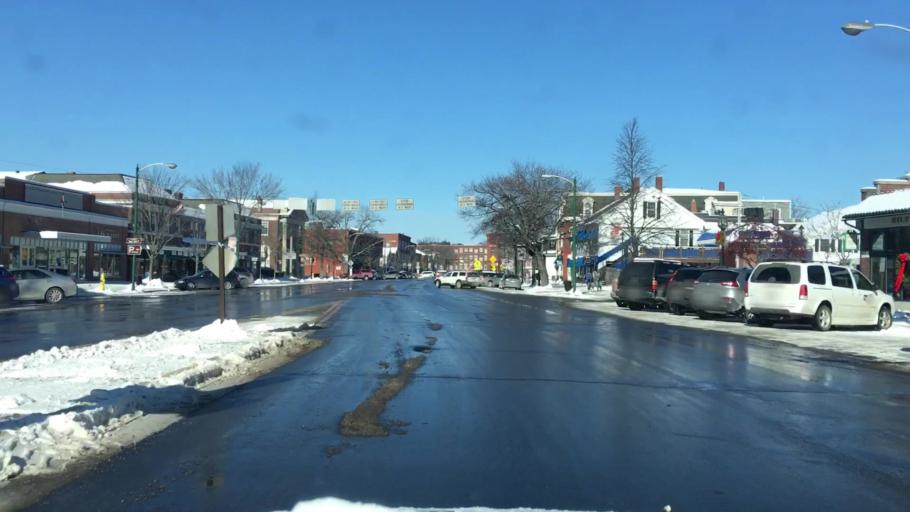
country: US
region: Maine
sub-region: Cumberland County
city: Brunswick
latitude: 43.9149
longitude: -69.9649
